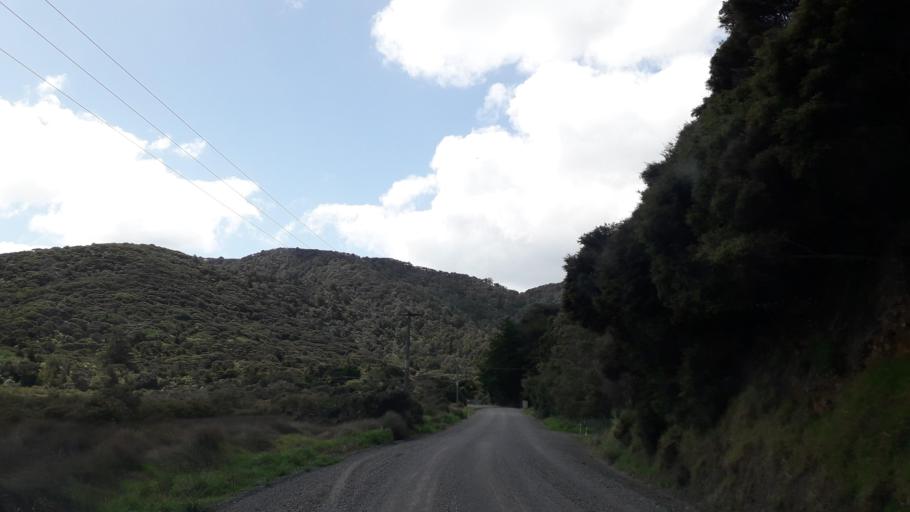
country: NZ
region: Northland
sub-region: Far North District
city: Paihia
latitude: -35.2585
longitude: 174.2665
